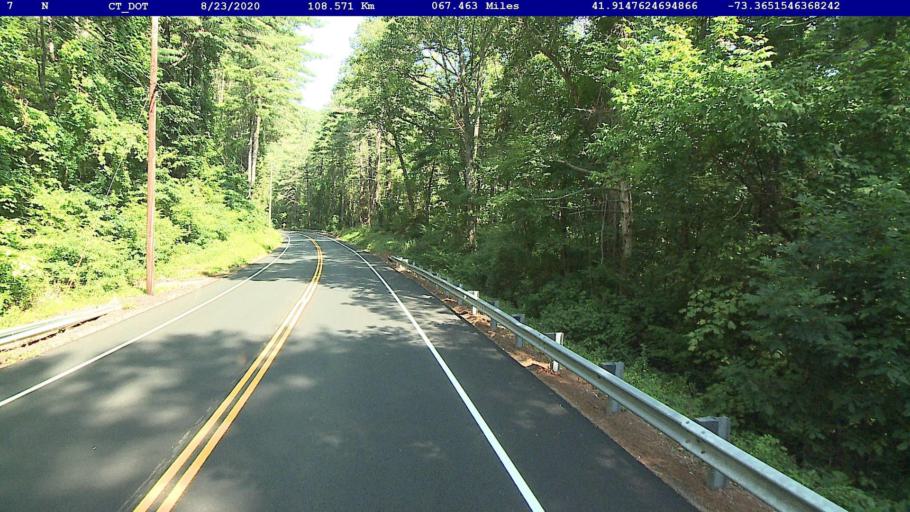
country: US
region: Connecticut
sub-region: Litchfield County
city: Canaan
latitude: 41.9148
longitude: -73.3652
